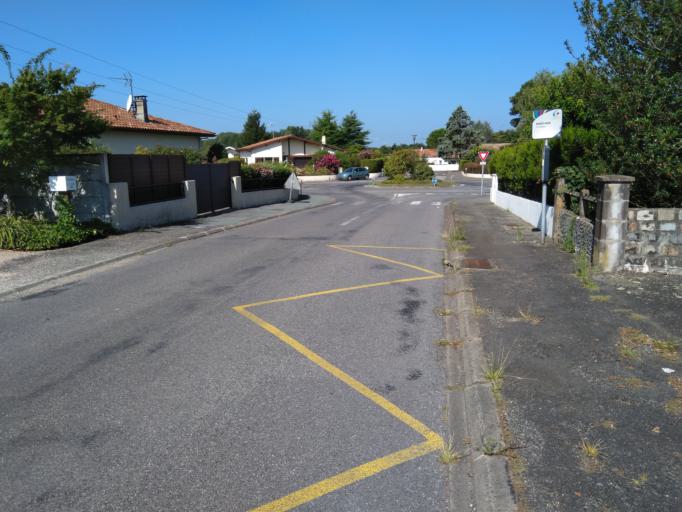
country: FR
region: Aquitaine
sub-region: Departement des Landes
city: Saint-Paul-les-Dax
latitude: 43.7367
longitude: -1.0585
